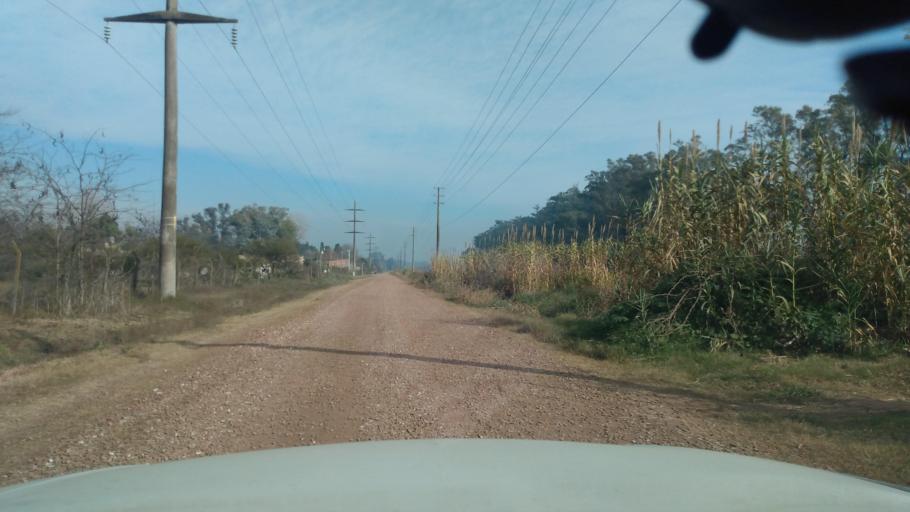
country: AR
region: Buenos Aires
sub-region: Partido de Lujan
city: Lujan
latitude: -34.5863
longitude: -59.1298
